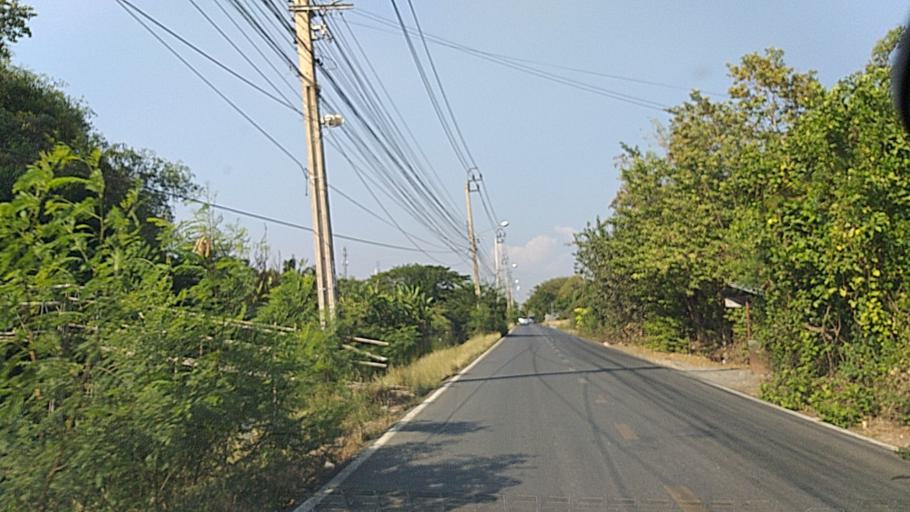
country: TH
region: Nonthaburi
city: Sai Noi
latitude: 13.9380
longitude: 100.3473
